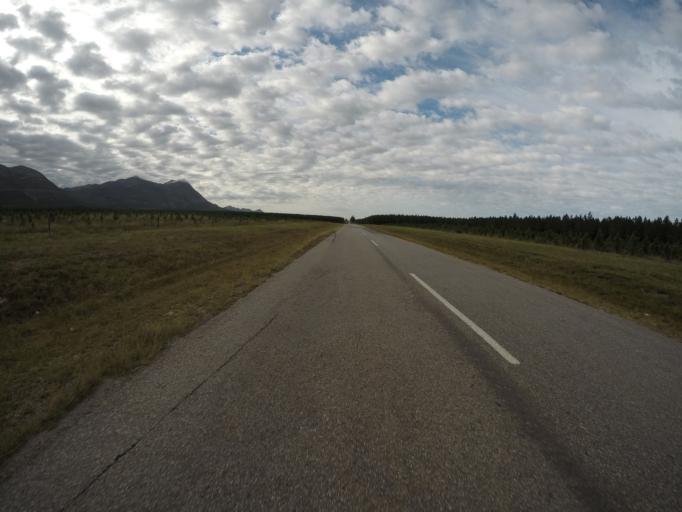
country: ZA
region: Eastern Cape
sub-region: Cacadu District Municipality
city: Kareedouw
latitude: -34.0304
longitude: 24.3806
